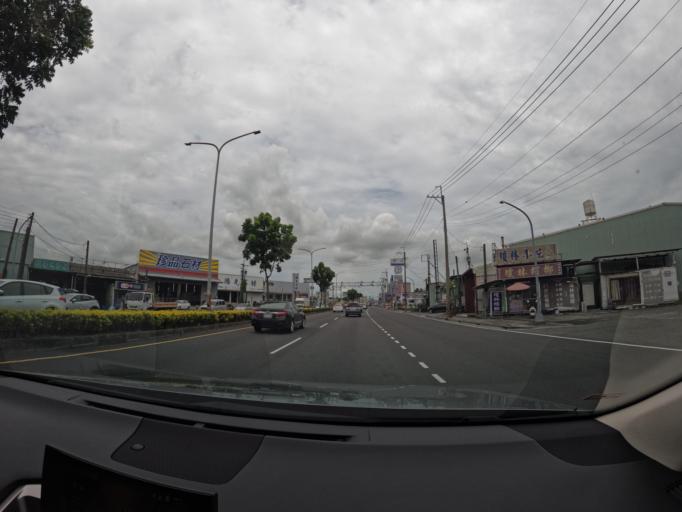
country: TW
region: Taiwan
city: Fengshan
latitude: 22.7873
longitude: 120.3184
